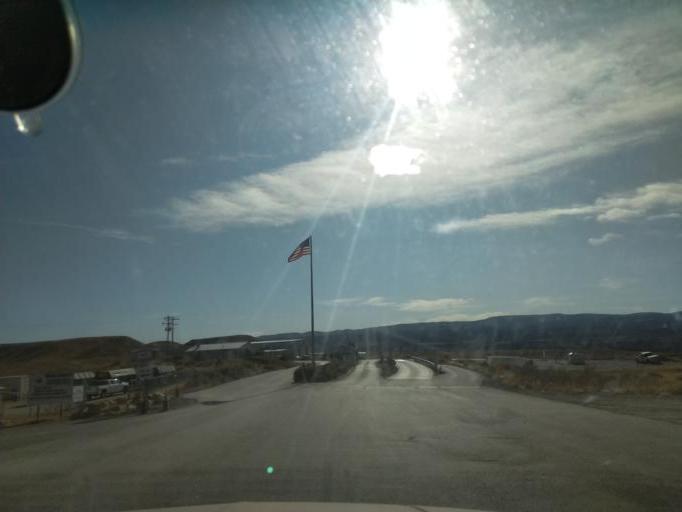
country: US
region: Colorado
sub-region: Mesa County
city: Fruitvale
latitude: 39.0104
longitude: -108.4849
